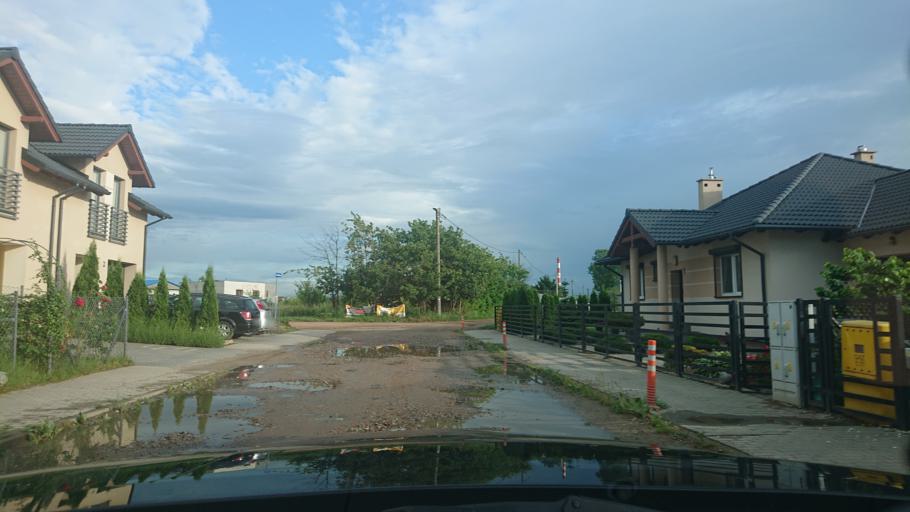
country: PL
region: Greater Poland Voivodeship
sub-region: Powiat gnieznienski
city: Gniezno
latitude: 52.5668
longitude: 17.6151
